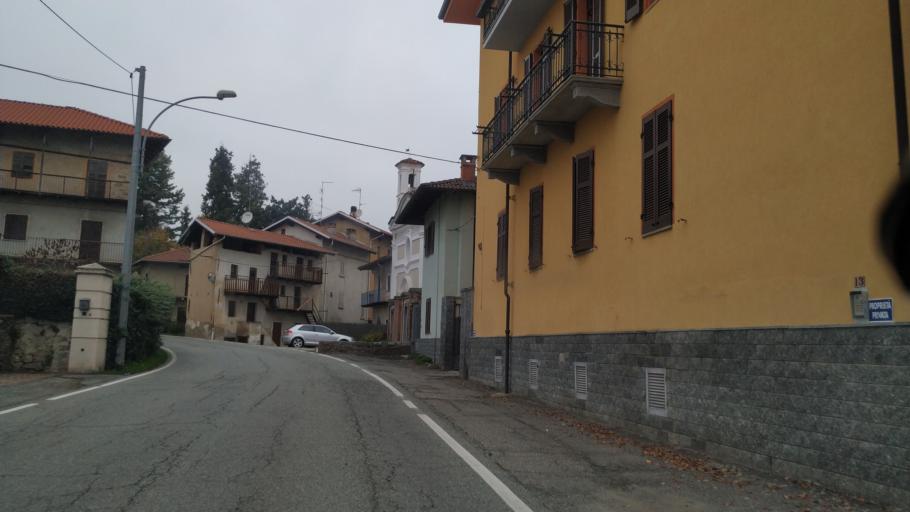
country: IT
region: Piedmont
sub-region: Provincia di Biella
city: Lessona
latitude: 45.5862
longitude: 8.1954
